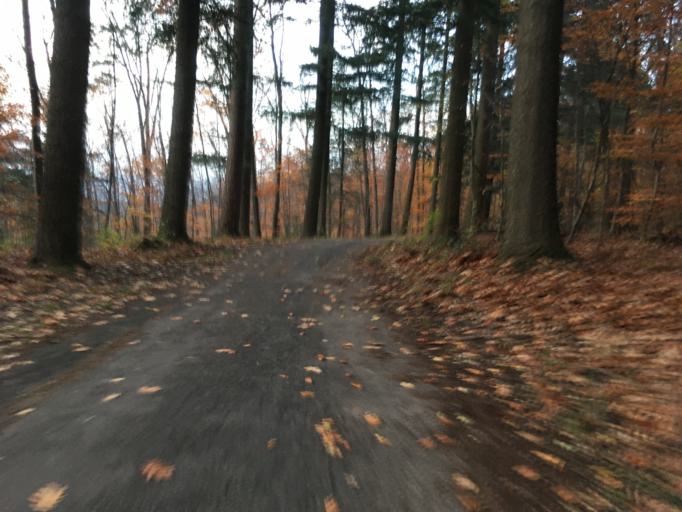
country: DE
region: Baden-Wuerttemberg
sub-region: Regierungsbezirk Stuttgart
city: Untergruppenbach
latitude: 49.1214
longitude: 9.2686
